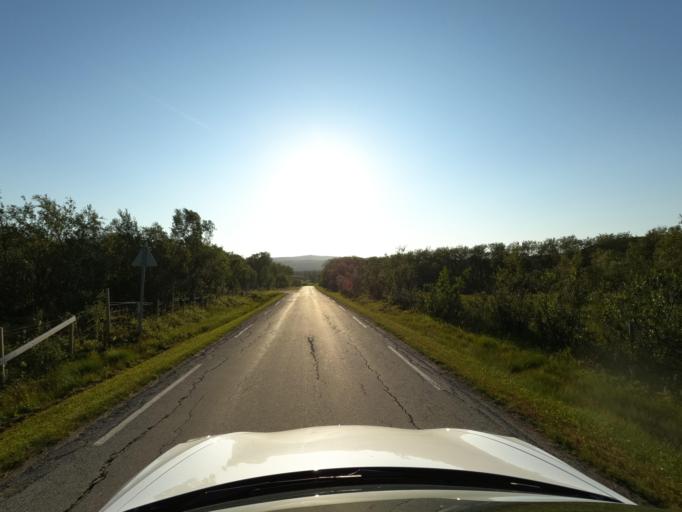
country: NO
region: Troms
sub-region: Skanland
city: Evenskjer
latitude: 68.4634
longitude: 16.6711
